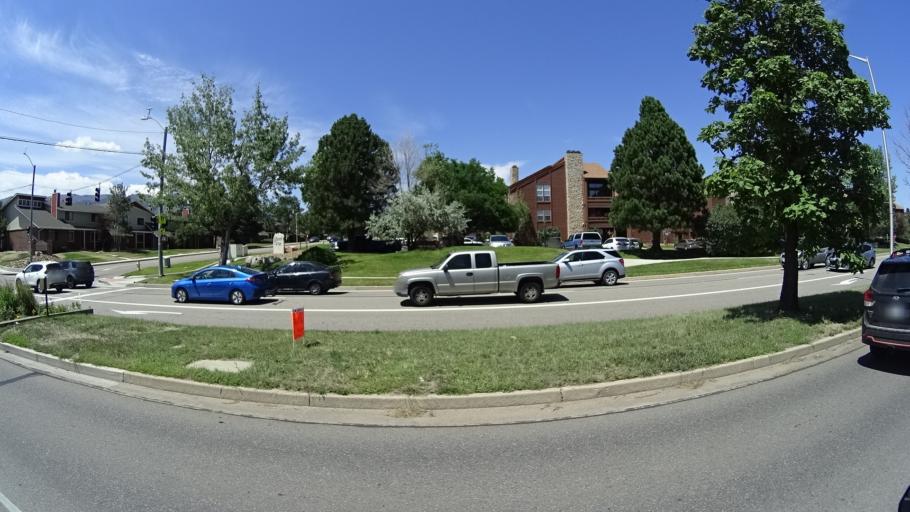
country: US
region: Colorado
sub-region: El Paso County
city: Air Force Academy
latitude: 38.9286
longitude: -104.8305
